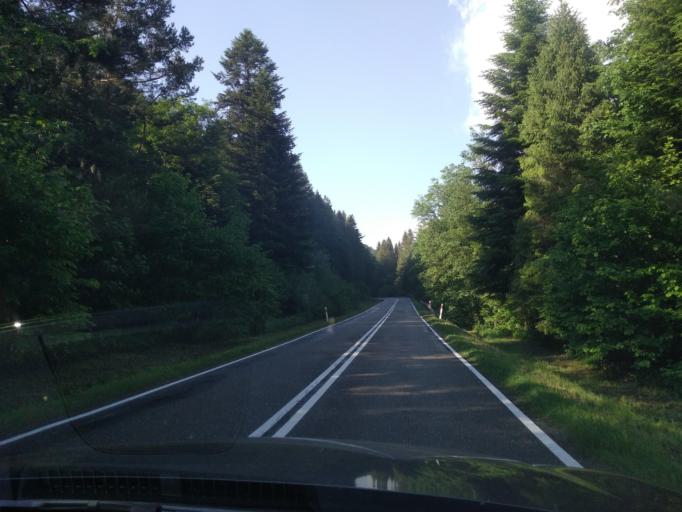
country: PL
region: Subcarpathian Voivodeship
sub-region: Powiat leski
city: Baligrod
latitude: 49.2941
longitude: 22.2686
